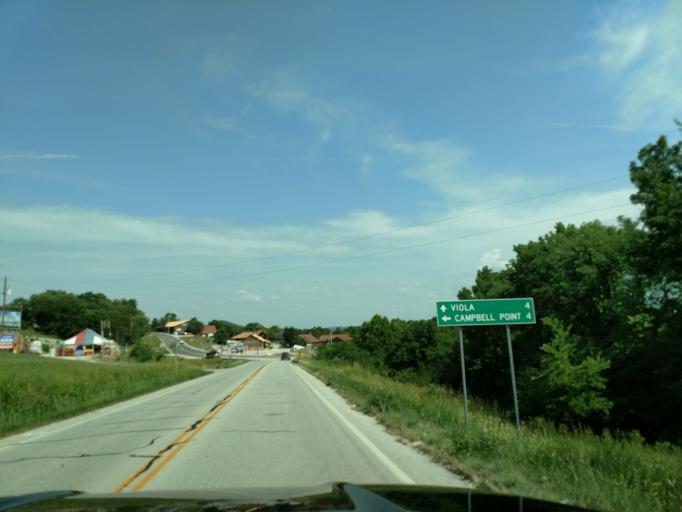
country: US
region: Missouri
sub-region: Barry County
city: Shell Knob
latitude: 36.6226
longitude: -93.6183
